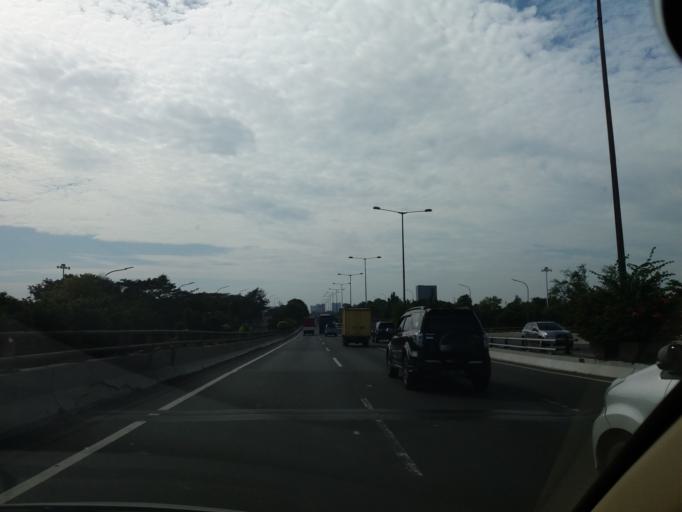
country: ID
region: Jakarta Raya
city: Jakarta
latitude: -6.2177
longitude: 106.8742
